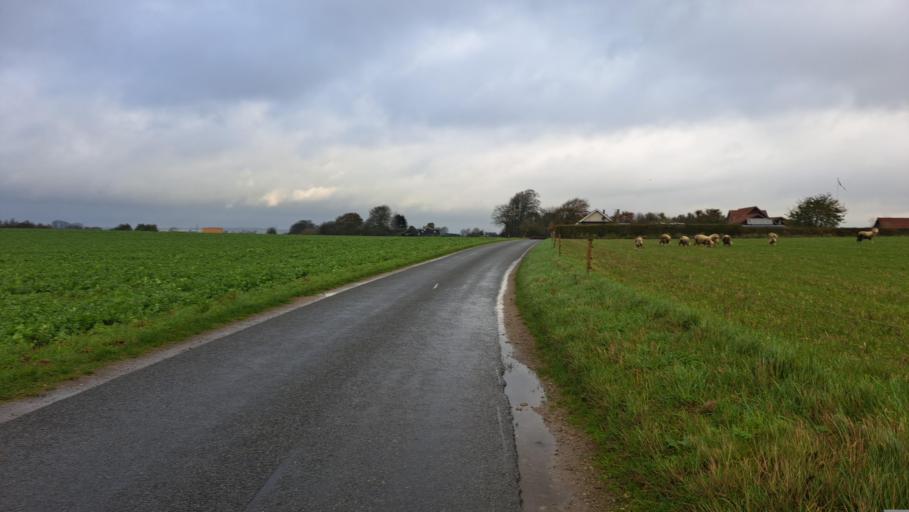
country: DK
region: Central Jutland
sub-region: Hedensted Kommune
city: Hedensted
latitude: 55.8340
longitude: 9.7357
